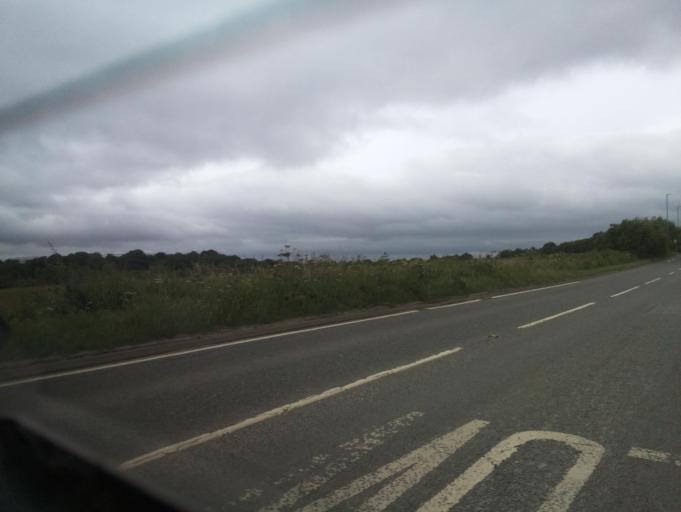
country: GB
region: England
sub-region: Leicestershire
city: Coalville
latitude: 52.7084
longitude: -1.3346
